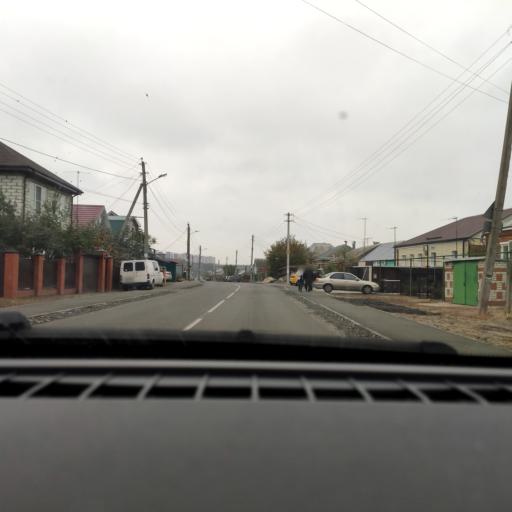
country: RU
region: Voronezj
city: Somovo
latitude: 51.7476
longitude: 39.3312
